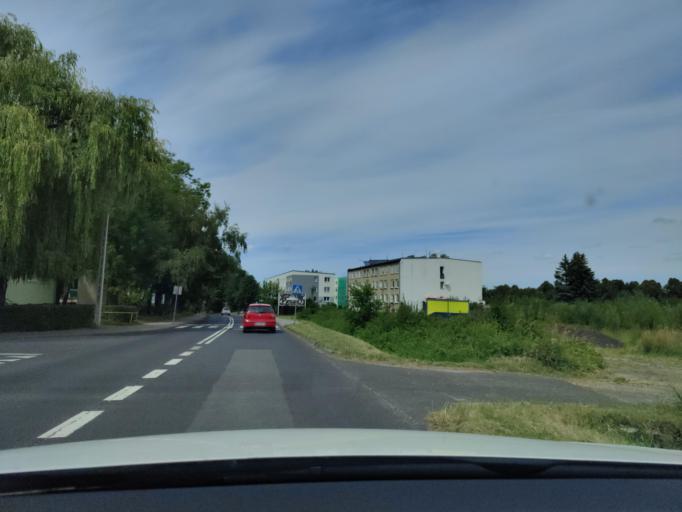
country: PL
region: Opole Voivodeship
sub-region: Powiat nyski
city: Glucholazy
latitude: 50.3070
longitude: 17.3914
